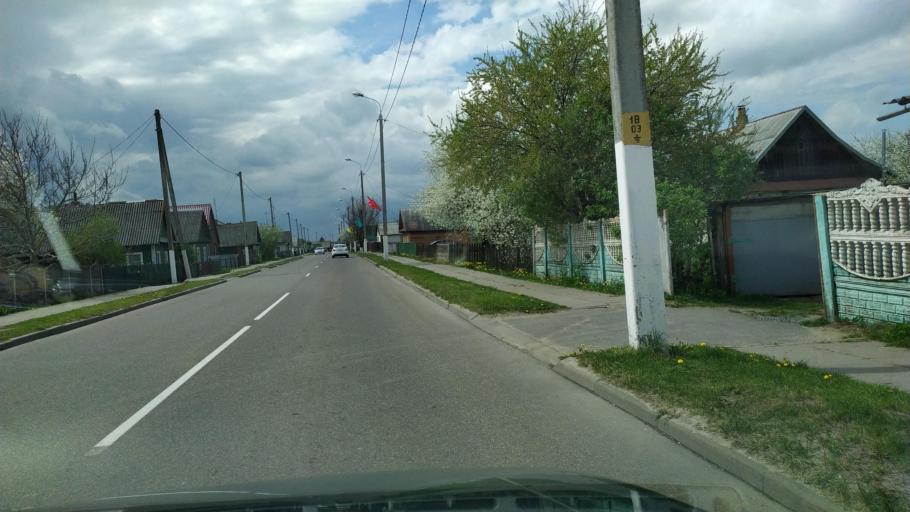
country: BY
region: Brest
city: Pruzhany
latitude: 52.5557
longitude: 24.4425
